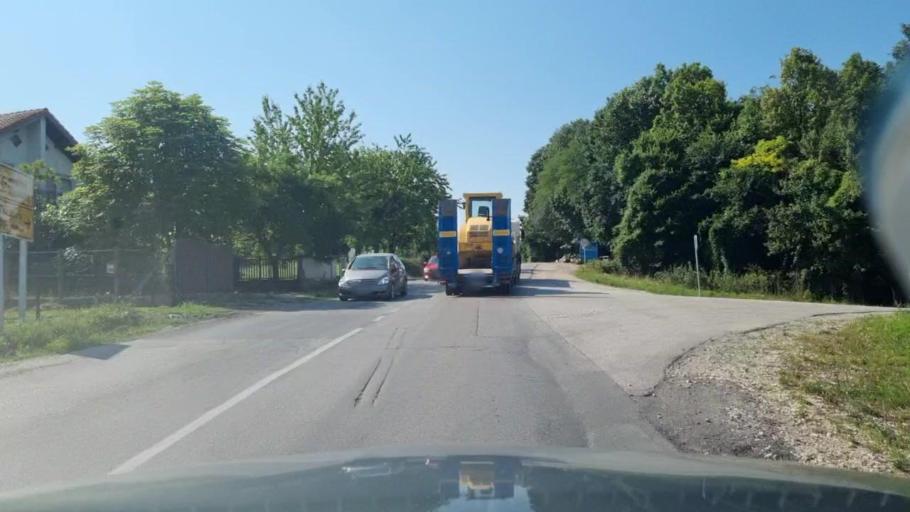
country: BA
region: Federation of Bosnia and Herzegovina
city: Gradacac
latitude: 44.8587
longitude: 18.4298
